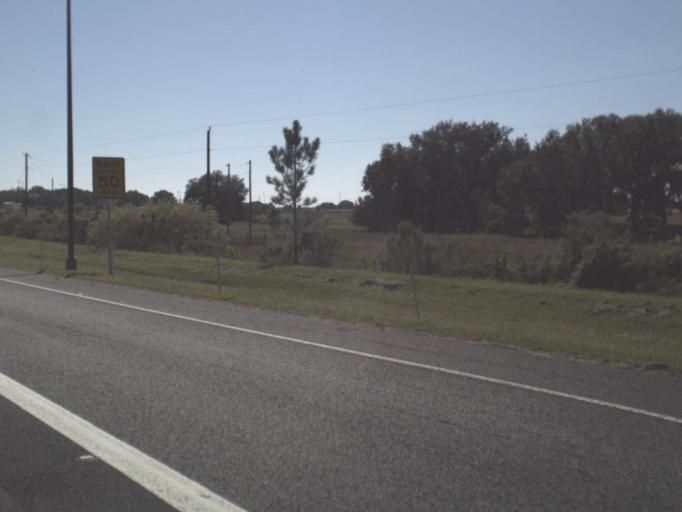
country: US
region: Florida
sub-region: Lake County
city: Hawthorne
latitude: 28.7608
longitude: -81.9446
